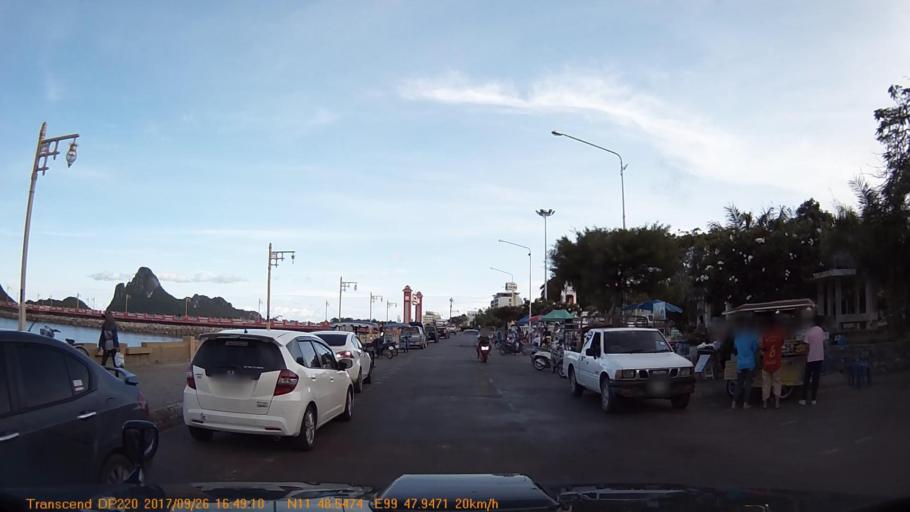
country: TH
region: Prachuap Khiri Khan
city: Prachuap Khiri Khan
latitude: 11.8091
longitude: 99.7991
